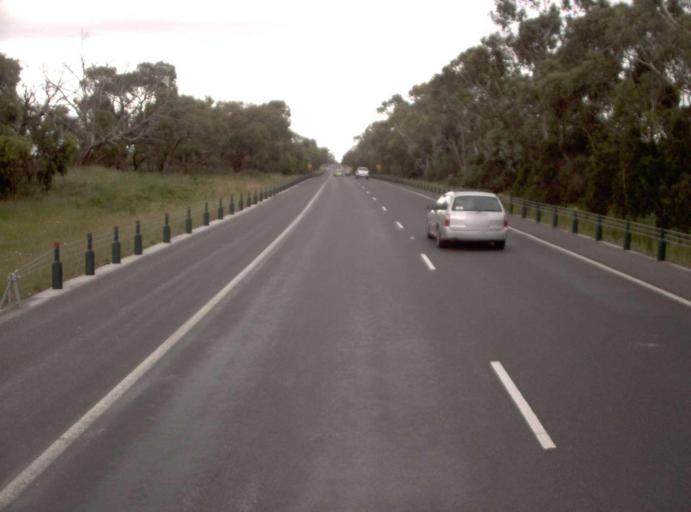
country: AU
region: Victoria
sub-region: Casey
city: Tooradin
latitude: -38.2174
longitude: 145.3995
